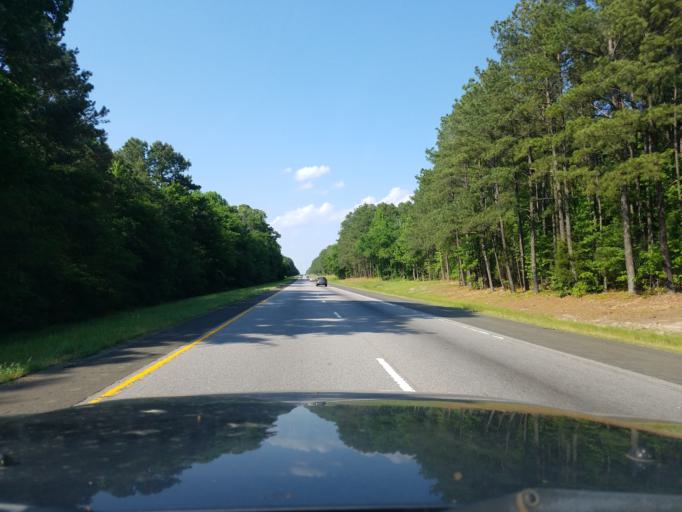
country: US
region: North Carolina
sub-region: Granville County
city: Butner
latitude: 36.0904
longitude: -78.7612
